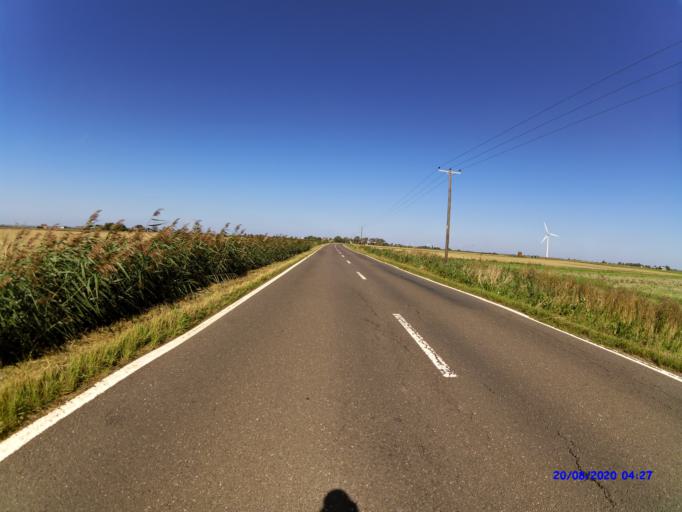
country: GB
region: England
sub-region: Cambridgeshire
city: Whittlesey
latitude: 52.5041
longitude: -0.1340
